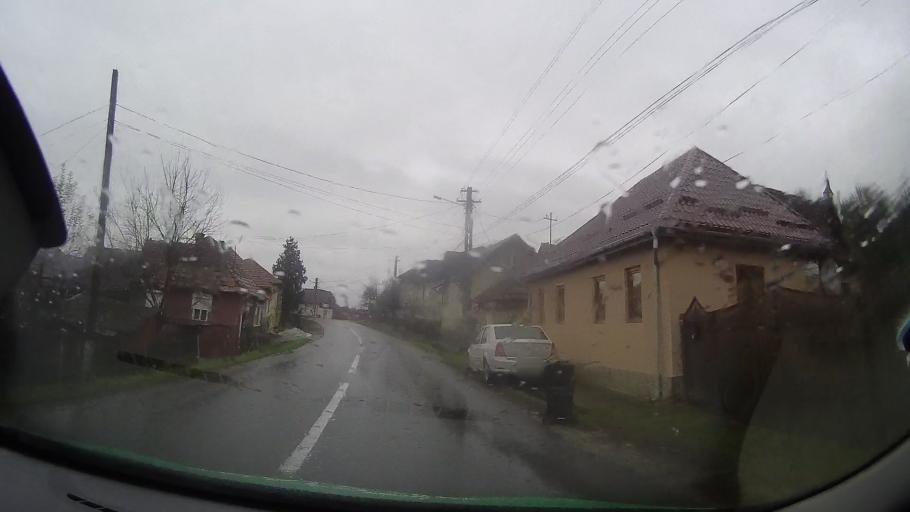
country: RO
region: Bistrita-Nasaud
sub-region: Comuna Mariselu
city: Mariselu
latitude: 47.0135
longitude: 24.5106
